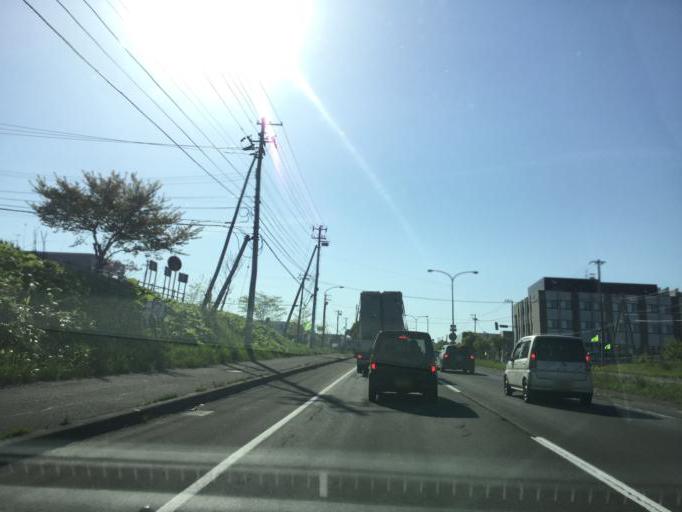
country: JP
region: Hokkaido
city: Kitahiroshima
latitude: 43.0160
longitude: 141.4958
